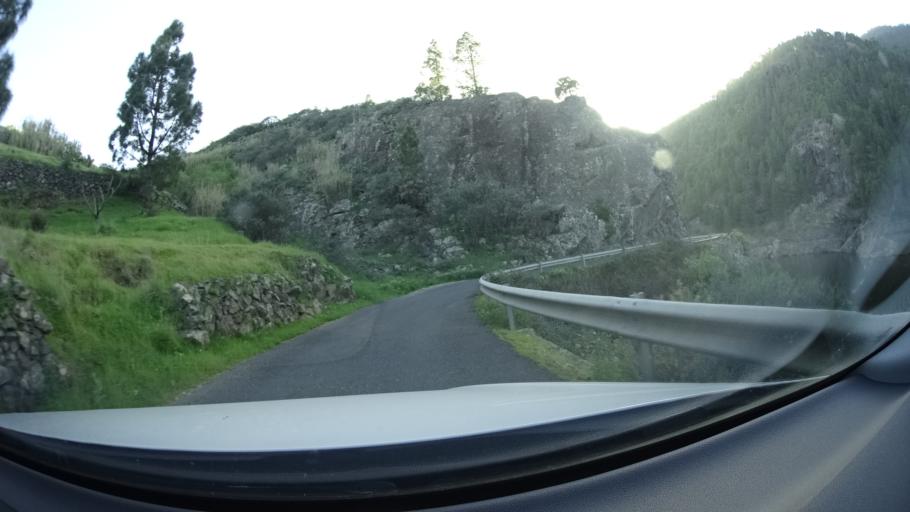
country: ES
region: Canary Islands
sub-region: Provincia de Las Palmas
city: Artenara
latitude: 28.0440
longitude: -15.6732
